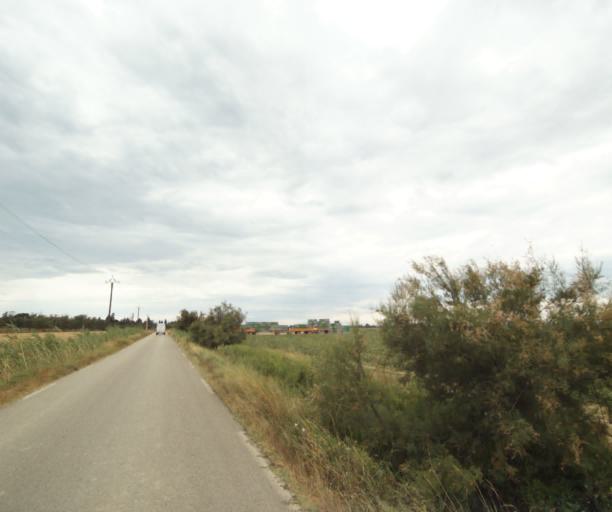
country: FR
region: Languedoc-Roussillon
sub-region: Departement de l'Herault
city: La Grande-Motte
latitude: 43.5972
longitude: 4.1180
